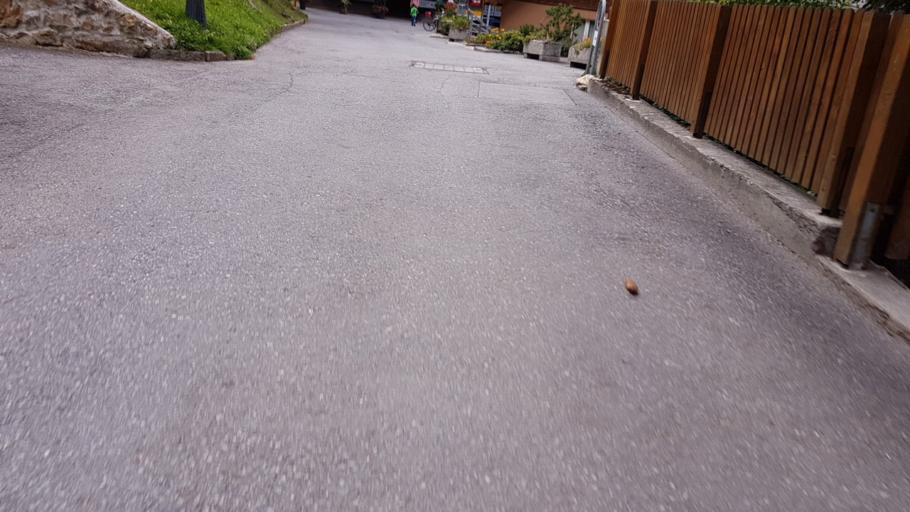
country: CH
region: Valais
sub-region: Leuk District
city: Leukerbad
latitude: 46.3744
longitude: 7.6295
